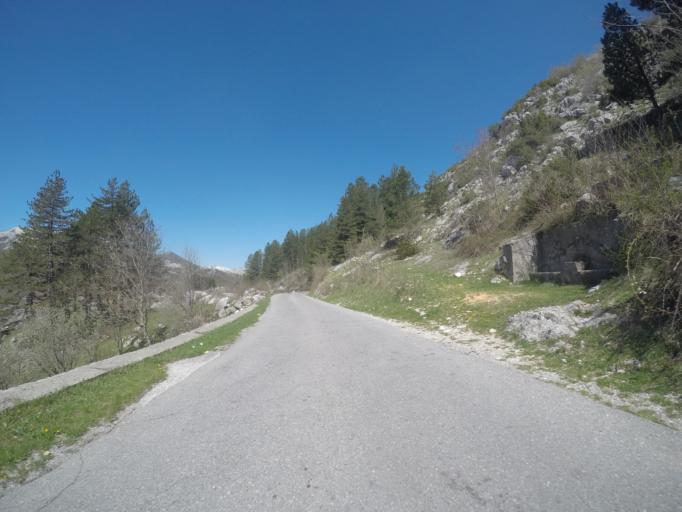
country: ME
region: Cetinje
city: Cetinje
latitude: 42.4652
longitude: 18.8609
